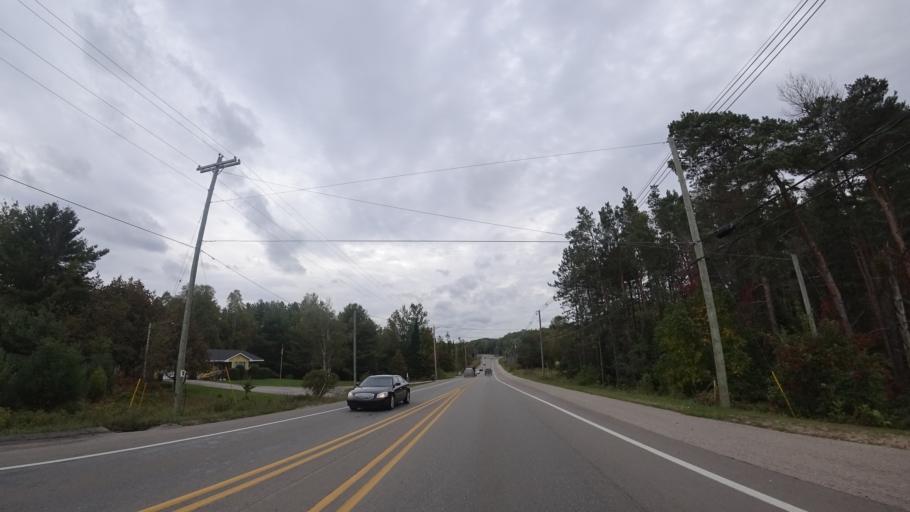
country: US
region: Michigan
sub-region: Emmet County
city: Petoskey
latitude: 45.4187
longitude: -84.9045
